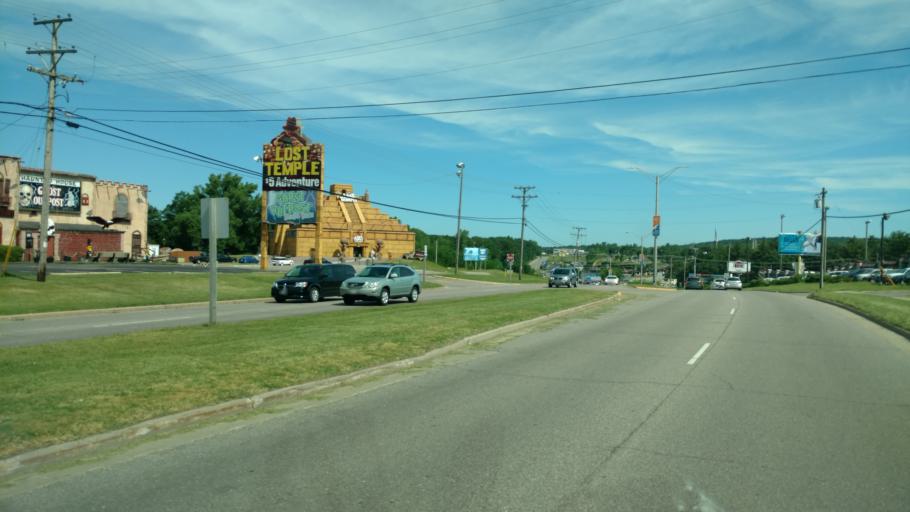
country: US
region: Wisconsin
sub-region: Columbia County
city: Wisconsin Dells
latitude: 43.6204
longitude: -89.7837
